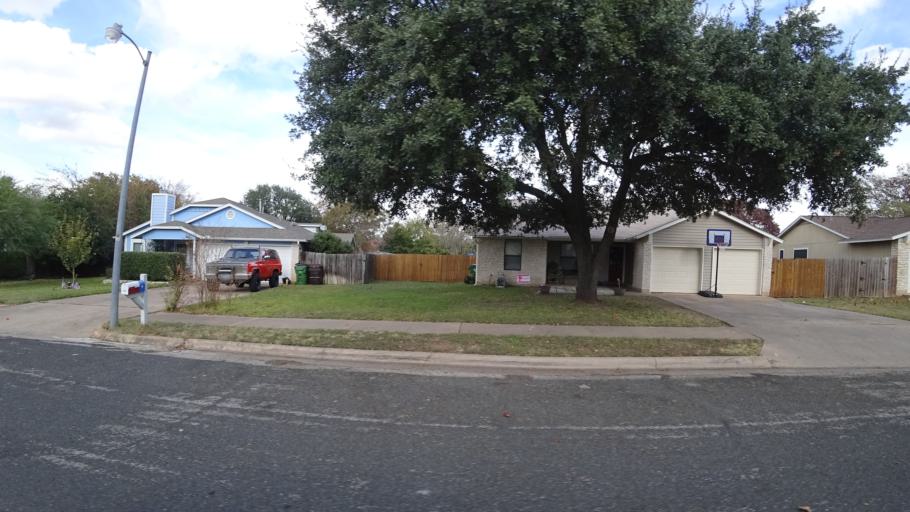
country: US
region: Texas
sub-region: Williamson County
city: Brushy Creek
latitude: 30.5112
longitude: -97.7336
